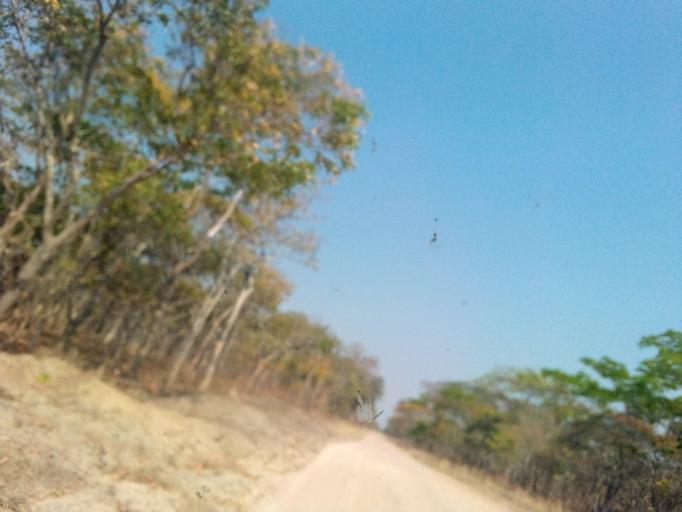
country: ZM
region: Northern
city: Mpika
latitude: -12.2283
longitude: 30.9119
